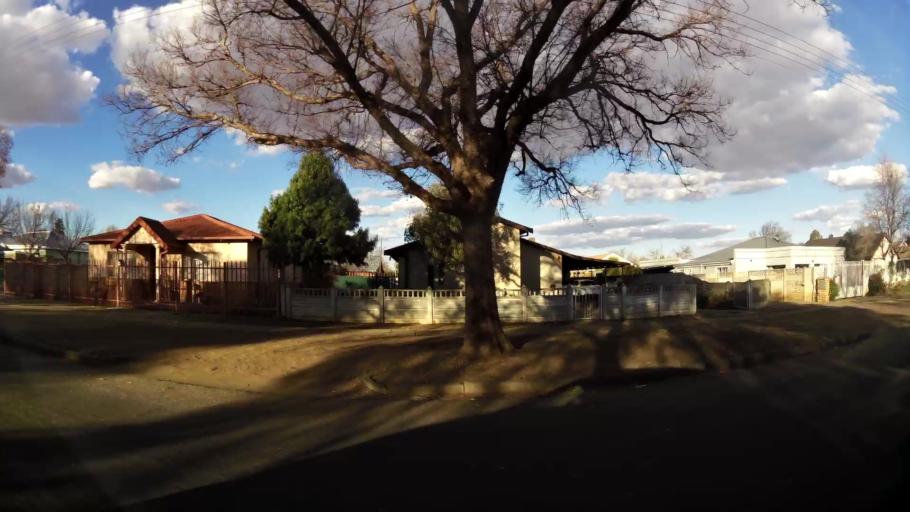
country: ZA
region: North-West
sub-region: Dr Kenneth Kaunda District Municipality
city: Potchefstroom
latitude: -26.7381
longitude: 27.0889
